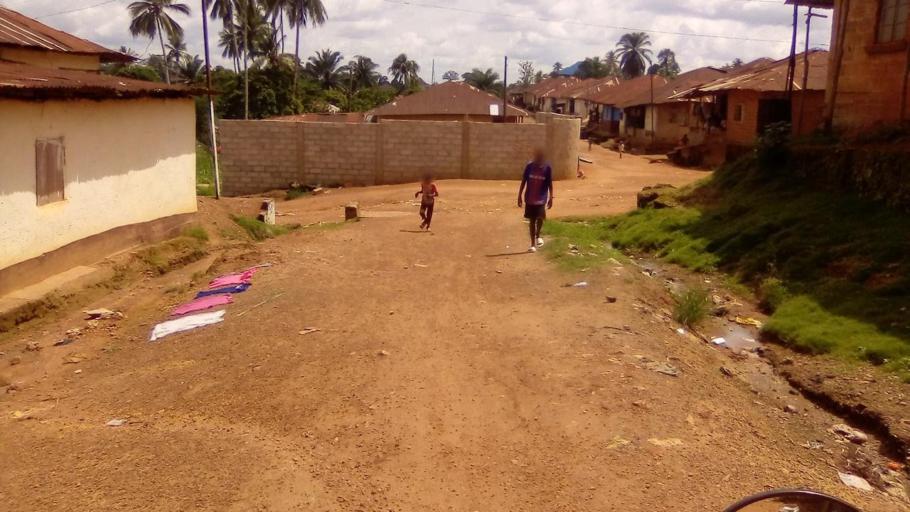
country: SL
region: Southern Province
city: Bo
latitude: 7.9677
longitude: -11.7318
